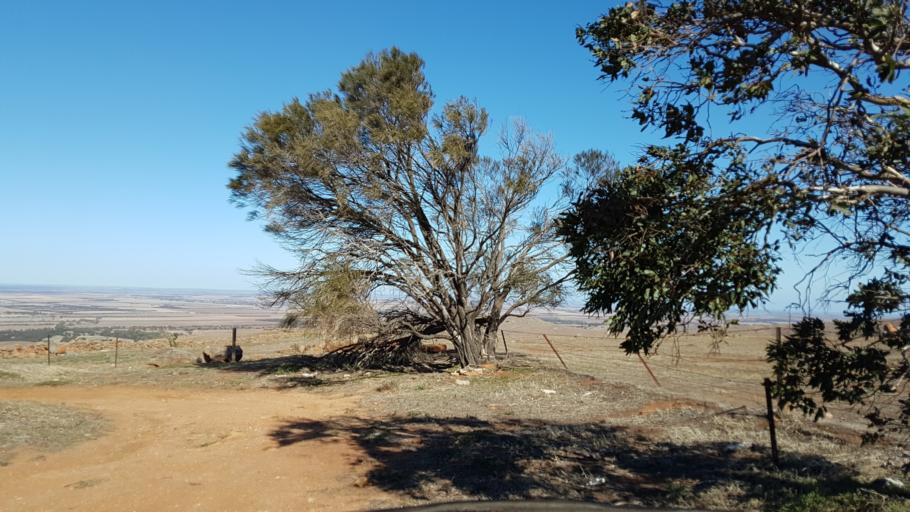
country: AU
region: South Australia
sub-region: Mid Murray
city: Mannum
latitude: -34.7590
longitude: 139.1826
